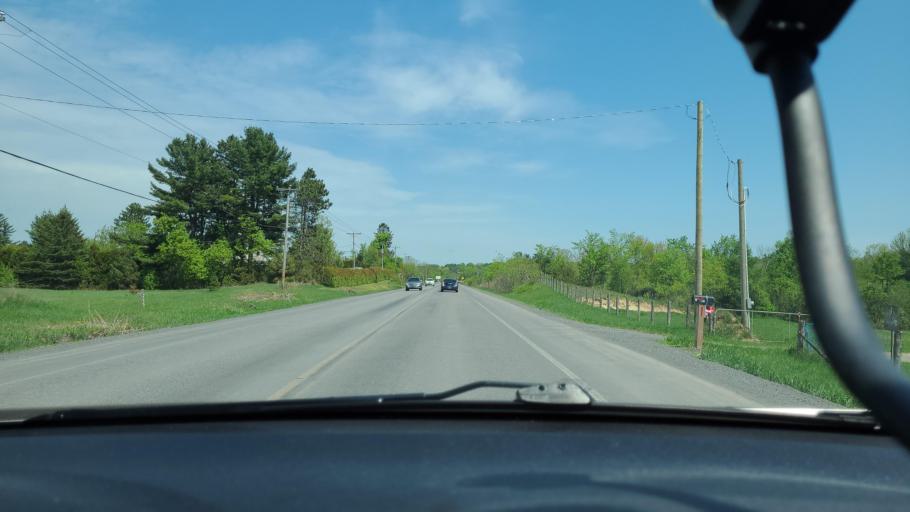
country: CA
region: Quebec
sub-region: Laurentides
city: Saint-Colomban
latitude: 45.6682
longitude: -74.2206
